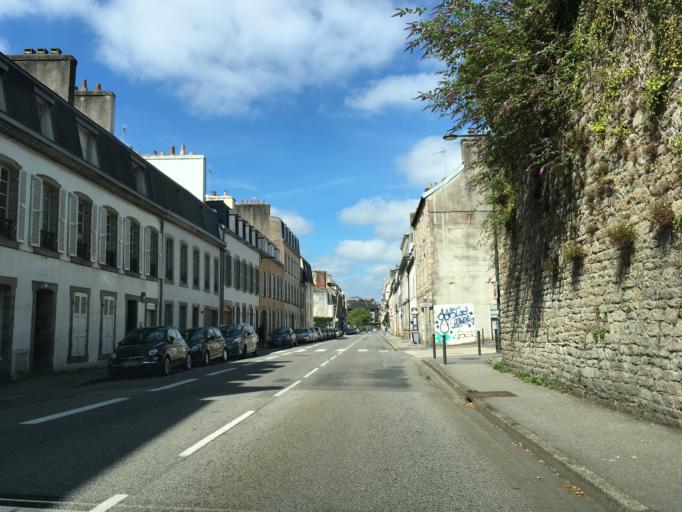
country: FR
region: Brittany
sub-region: Departement du Finistere
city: Quimper
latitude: 47.9977
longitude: -4.0970
